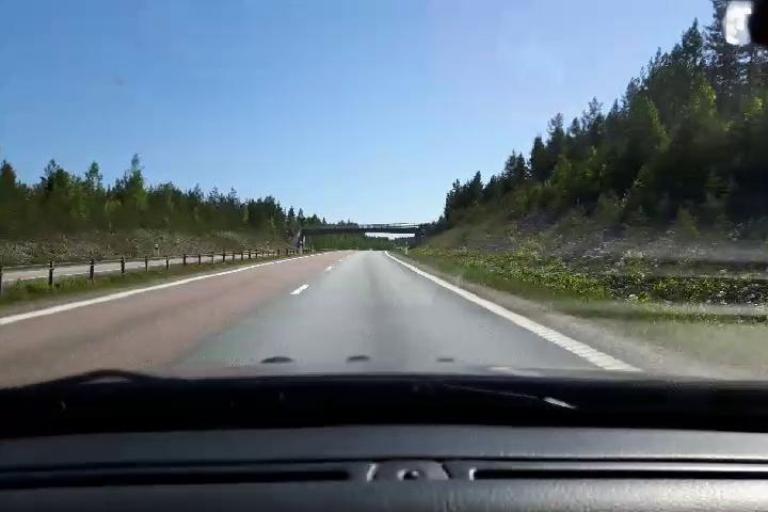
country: SE
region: Gaevleborg
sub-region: Soderhamns Kommun
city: Soderhamn
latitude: 61.4700
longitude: 16.9900
